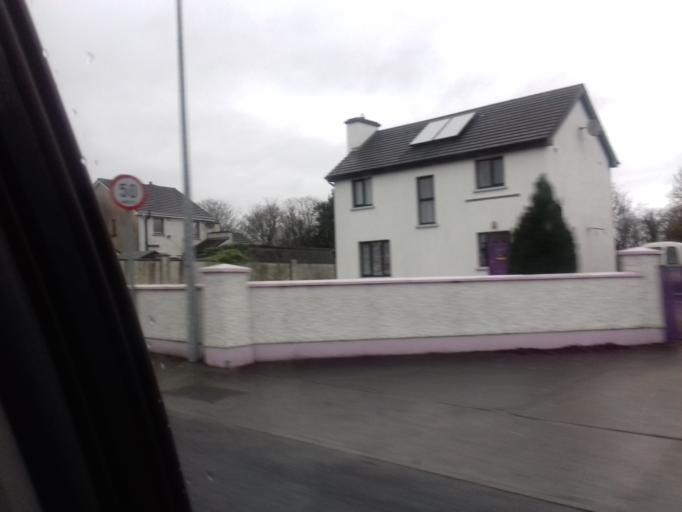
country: IE
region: Leinster
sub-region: County Carlow
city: Bagenalstown
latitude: 52.6789
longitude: -7.0203
